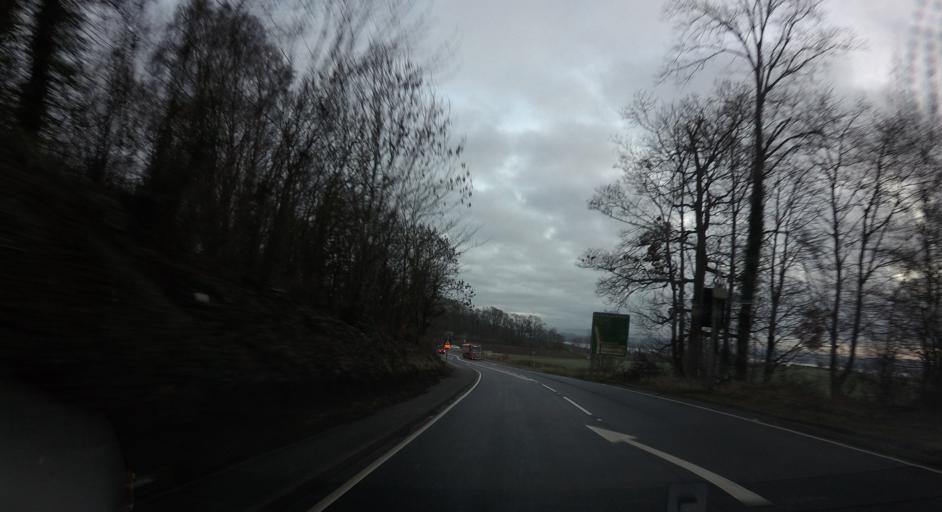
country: GB
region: Scotland
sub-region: Fife
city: Limekilns
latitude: 56.0395
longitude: -3.4707
